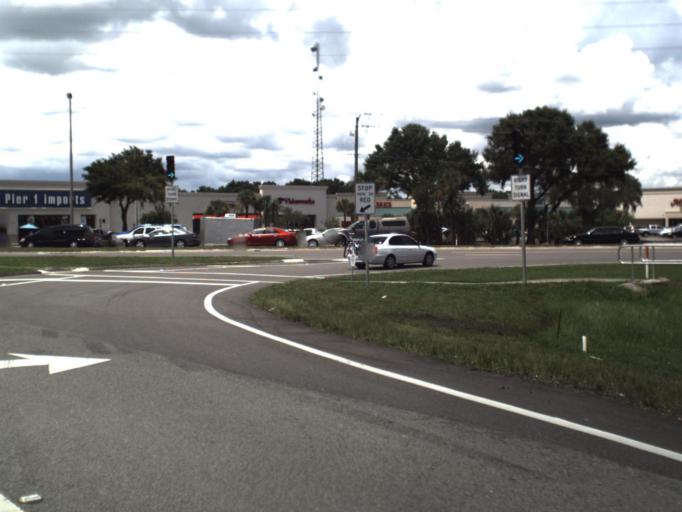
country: US
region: Florida
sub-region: Charlotte County
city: Port Charlotte
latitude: 27.0127
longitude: -82.1453
